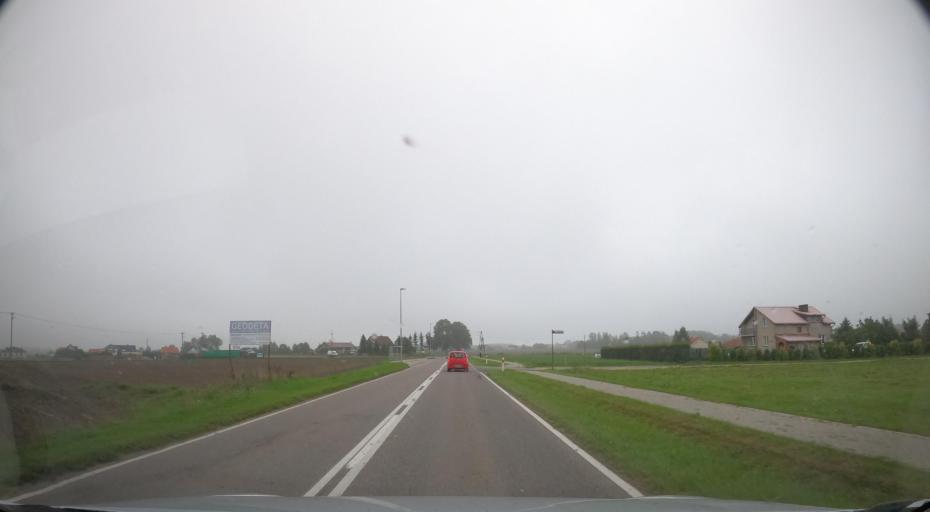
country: PL
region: Pomeranian Voivodeship
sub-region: Powiat wejherowski
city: Bojano
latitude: 54.4521
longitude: 18.3709
